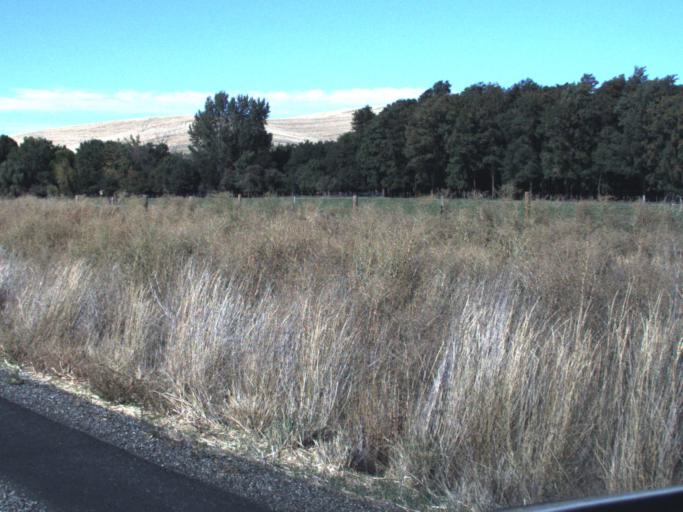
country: US
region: Washington
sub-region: Walla Walla County
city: Waitsburg
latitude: 46.2942
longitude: -118.2684
